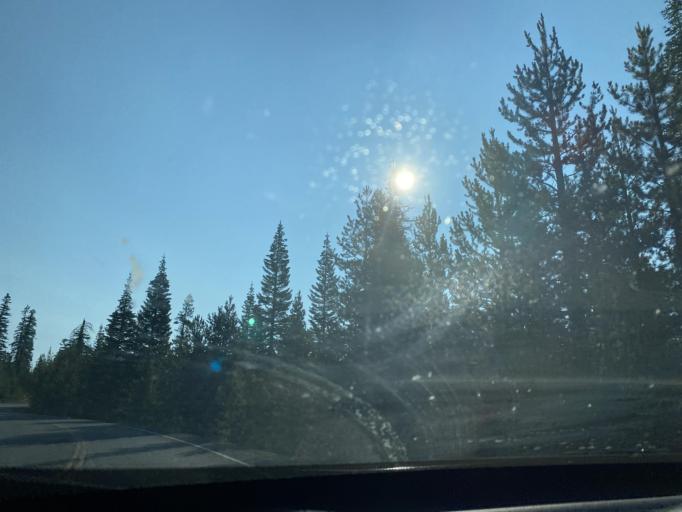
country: US
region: Oregon
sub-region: Deschutes County
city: La Pine
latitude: 43.7029
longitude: -121.3144
